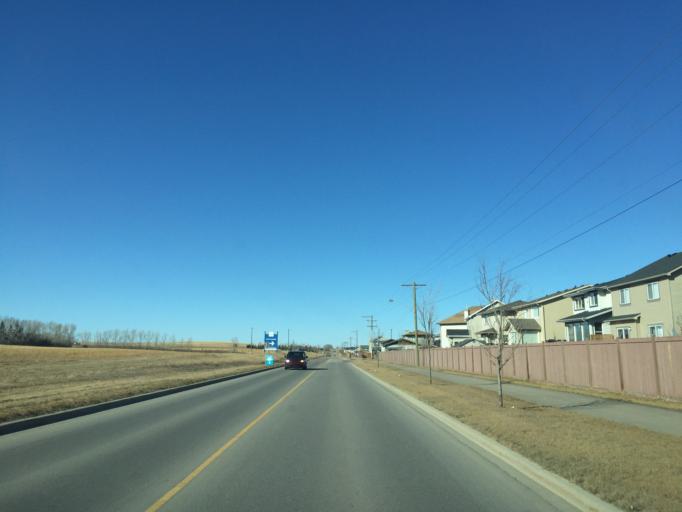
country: CA
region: Alberta
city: Airdrie
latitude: 51.2864
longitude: -114.0485
